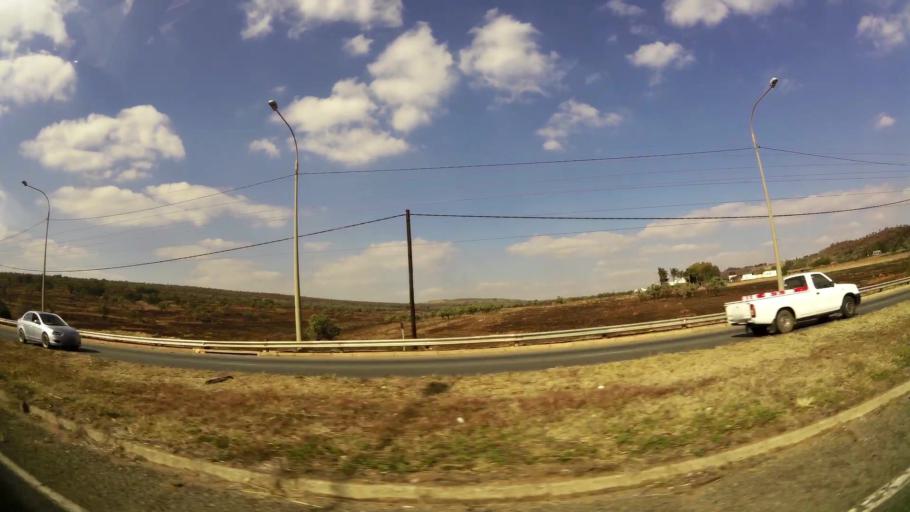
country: ZA
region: Gauteng
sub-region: West Rand District Municipality
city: Krugersdorp
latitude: -26.0687
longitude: 27.8033
